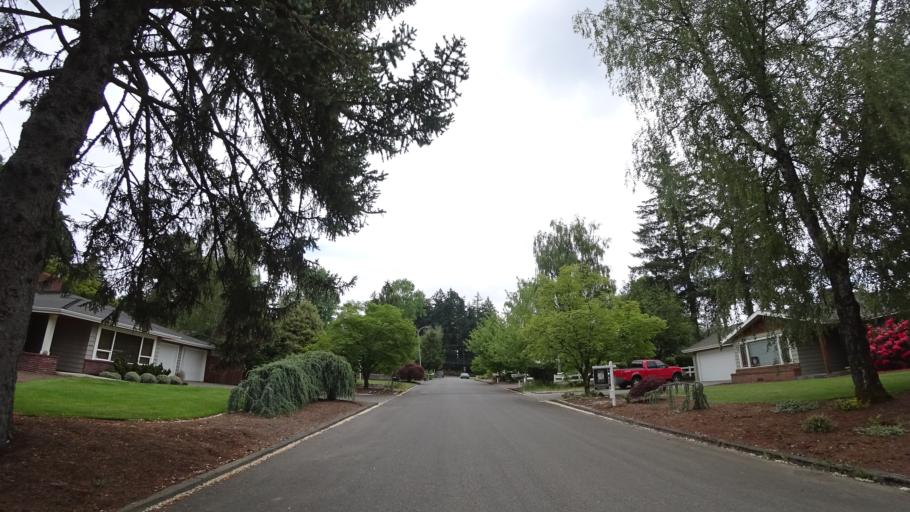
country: US
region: Oregon
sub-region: Washington County
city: Garden Home-Whitford
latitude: 45.4592
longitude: -122.7832
